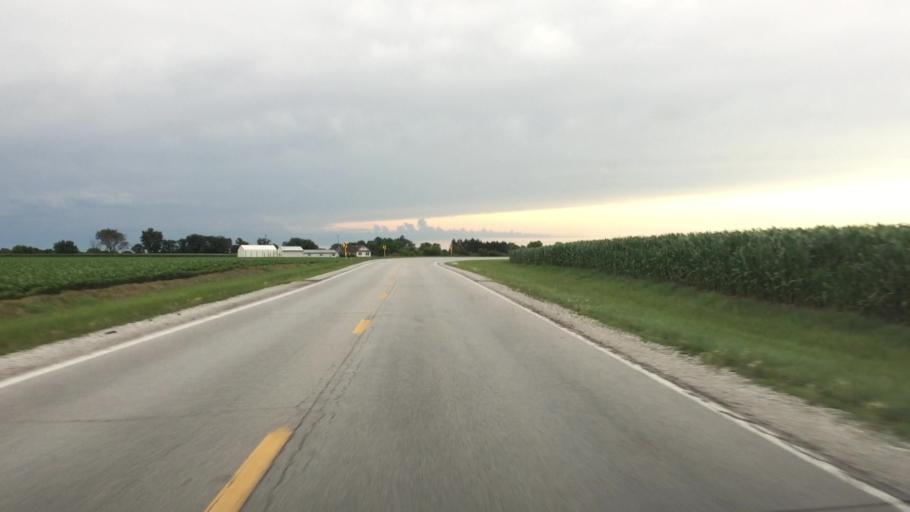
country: US
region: Illinois
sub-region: Hancock County
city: Hamilton
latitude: 40.3674
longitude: -91.3422
